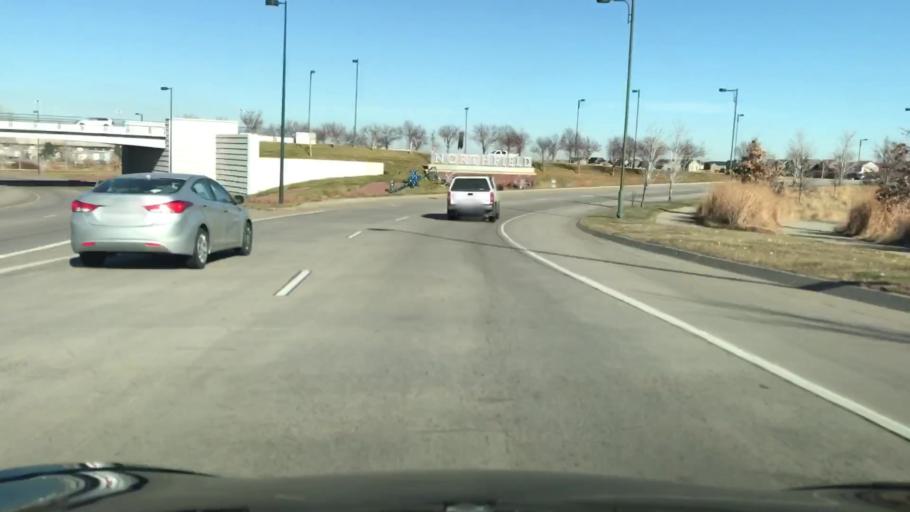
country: US
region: Colorado
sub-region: Adams County
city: Commerce City
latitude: 39.7845
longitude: -104.8995
